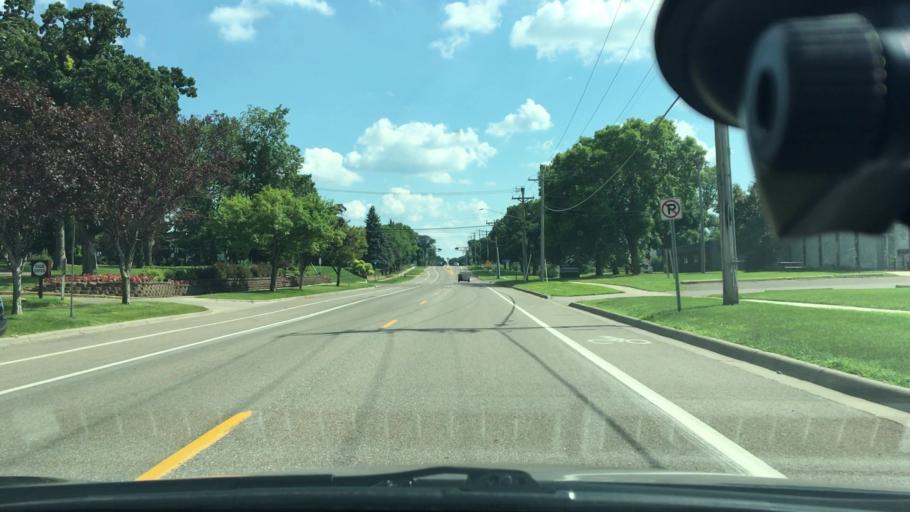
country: US
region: Minnesota
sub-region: Hennepin County
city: New Hope
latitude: 45.0520
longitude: -93.3907
